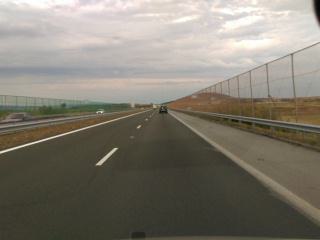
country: BG
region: Yambol
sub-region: Obshtina Yambol
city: Yambol
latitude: 42.5411
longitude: 26.4318
